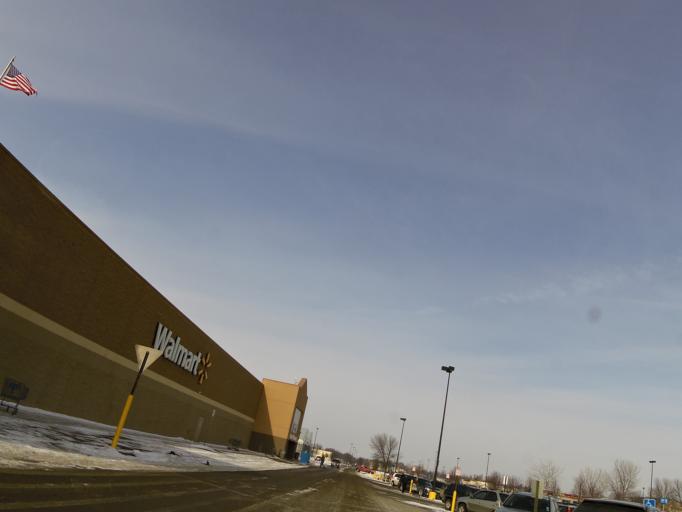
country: US
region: Minnesota
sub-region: McLeod County
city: Hutchinson
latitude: 44.8714
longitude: -94.3780
